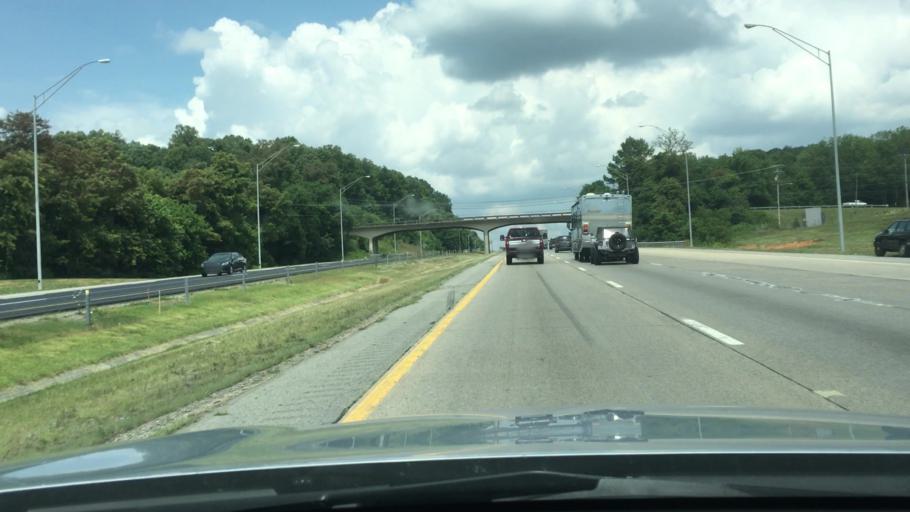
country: US
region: Tennessee
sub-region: Washington County
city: Oak Grove
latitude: 36.3582
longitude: -82.4013
